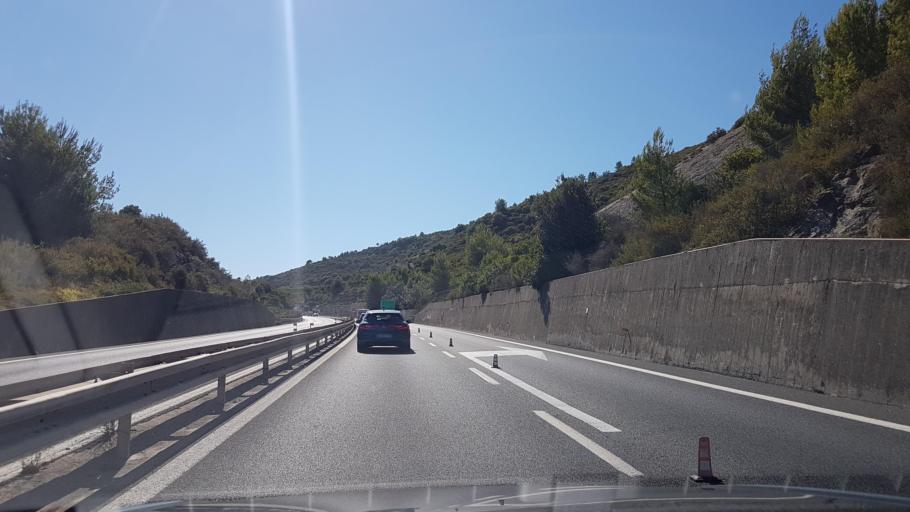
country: IT
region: Liguria
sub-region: Provincia di Imperia
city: Ospedaletti
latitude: 43.8022
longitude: 7.6956
